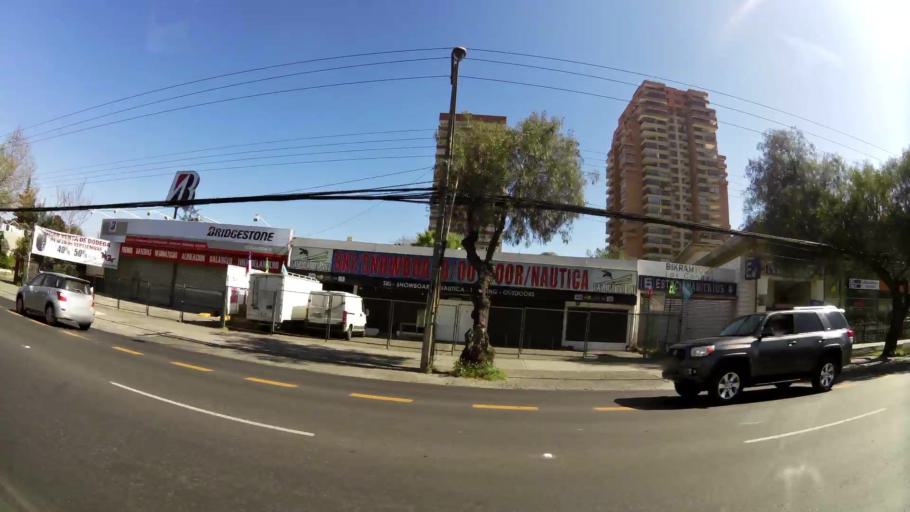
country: CL
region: Santiago Metropolitan
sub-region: Provincia de Santiago
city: Villa Presidente Frei, Nunoa, Santiago, Chile
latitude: -33.3932
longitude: -70.5442
